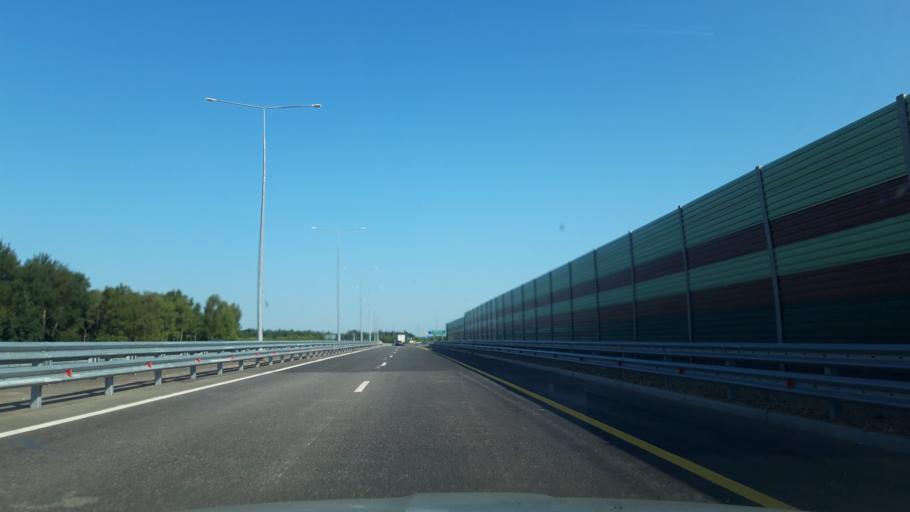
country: RU
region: Moskovskaya
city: Spas-Zaulok
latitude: 56.4919
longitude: 36.5315
